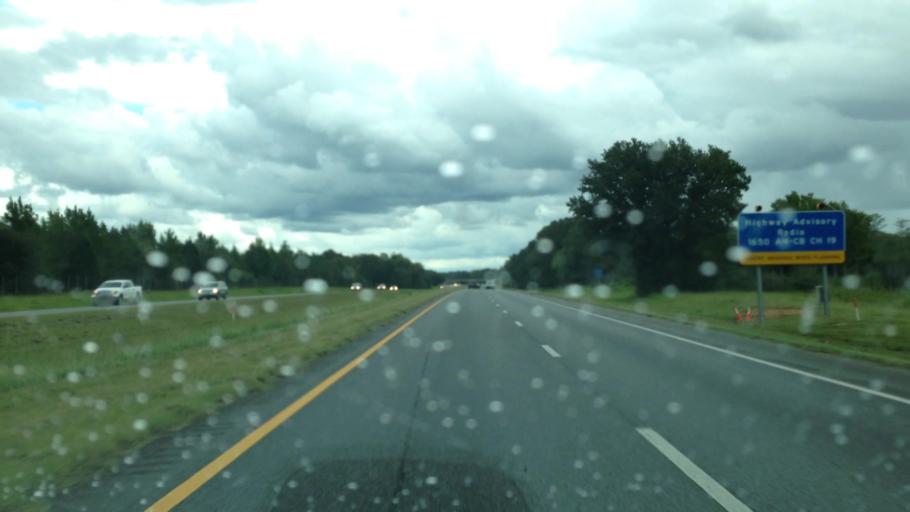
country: US
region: Florida
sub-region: Washington County
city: Chipley
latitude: 30.7463
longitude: -85.4268
